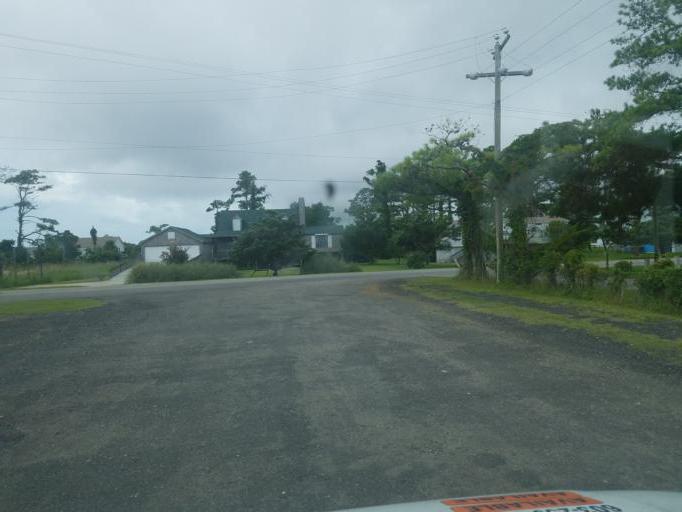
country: US
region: North Carolina
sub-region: Dare County
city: Wanchese
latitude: 35.8419
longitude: -75.6234
